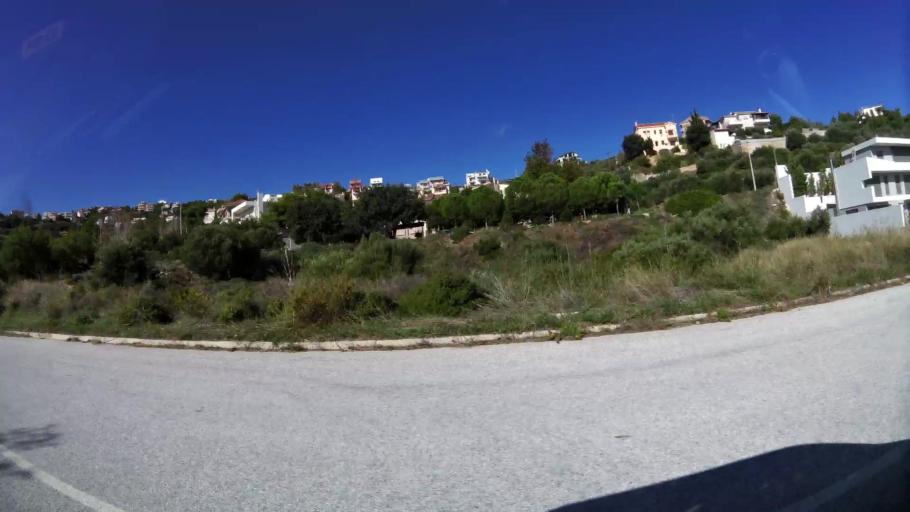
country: GR
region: Attica
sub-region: Nomarchia Anatolikis Attikis
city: Dhrafi
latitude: 38.0315
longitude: 23.9009
